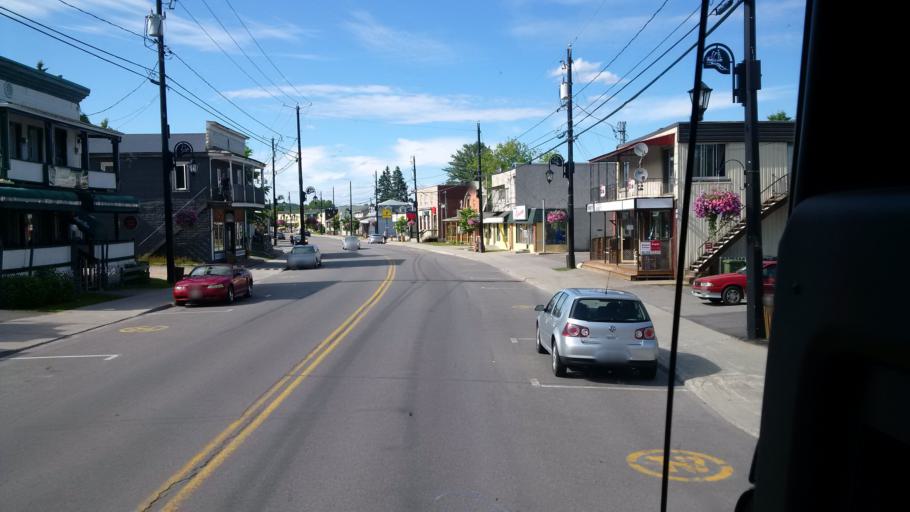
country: CA
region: Quebec
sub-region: Laurentides
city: Riviere-Rouge
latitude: 46.4115
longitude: -74.8704
